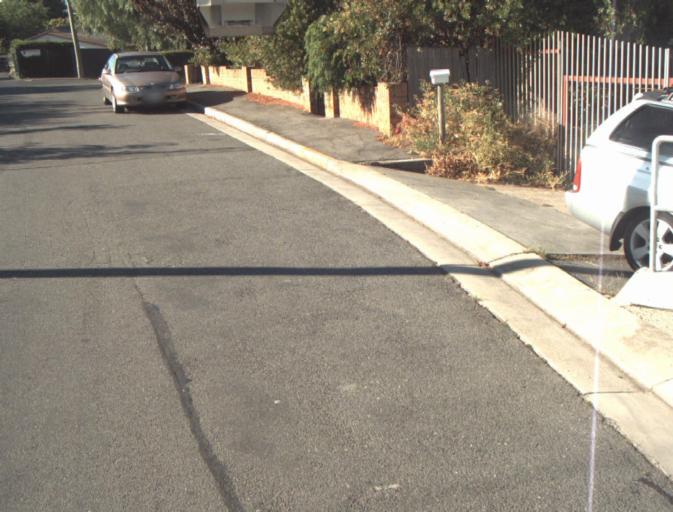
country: AU
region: Tasmania
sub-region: Launceston
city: Newnham
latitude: -41.4063
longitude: 147.1254
